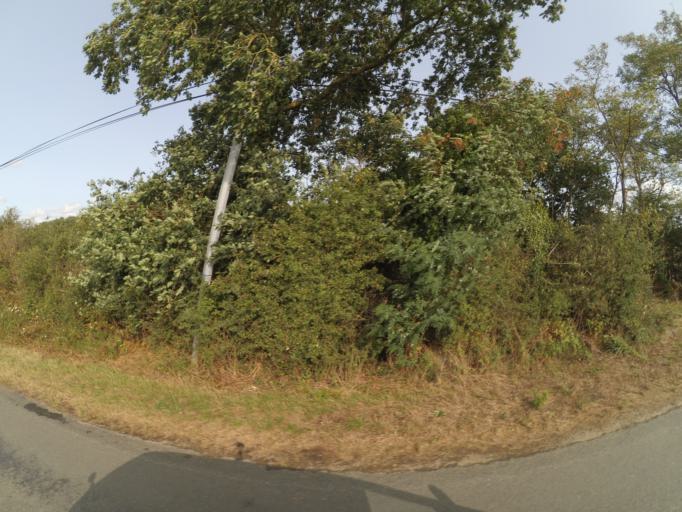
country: FR
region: Pays de la Loire
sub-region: Departement de la Vendee
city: La Bruffiere
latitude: 47.0013
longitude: -1.2008
